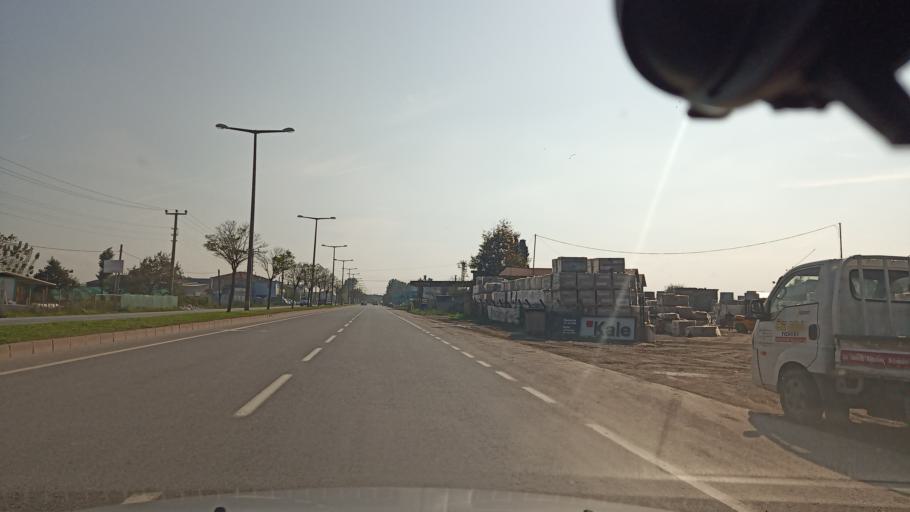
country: TR
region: Sakarya
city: Adapazari
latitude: 40.8177
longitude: 30.4001
